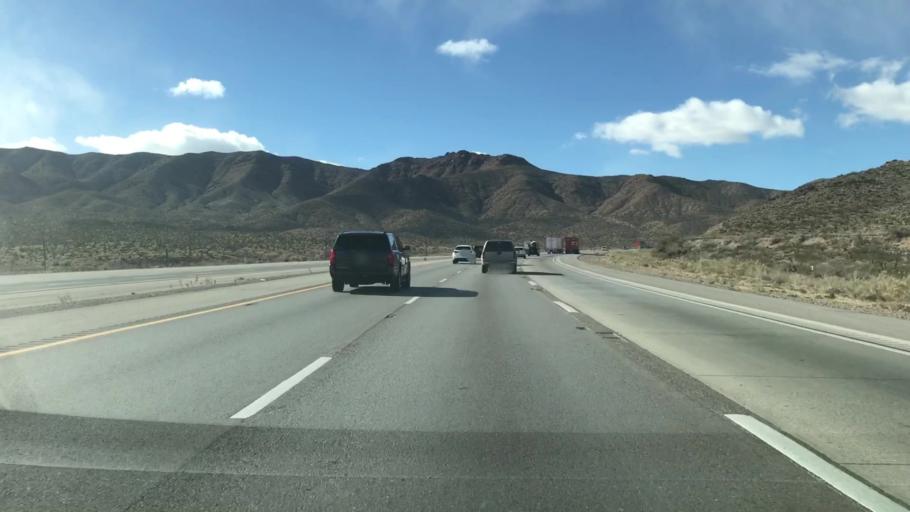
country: US
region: Nevada
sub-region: Clark County
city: Sandy Valley
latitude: 35.4628
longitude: -115.4646
